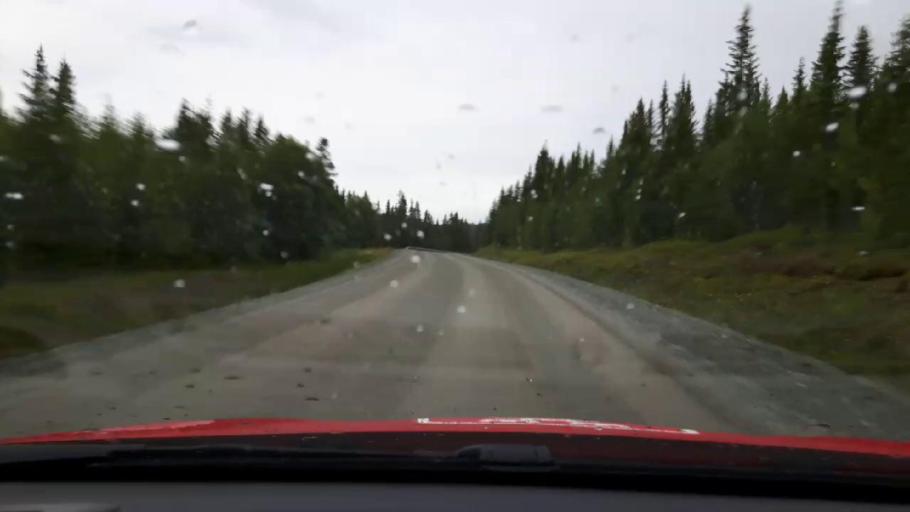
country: SE
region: Jaemtland
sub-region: Are Kommun
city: Are
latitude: 63.4428
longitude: 12.6951
